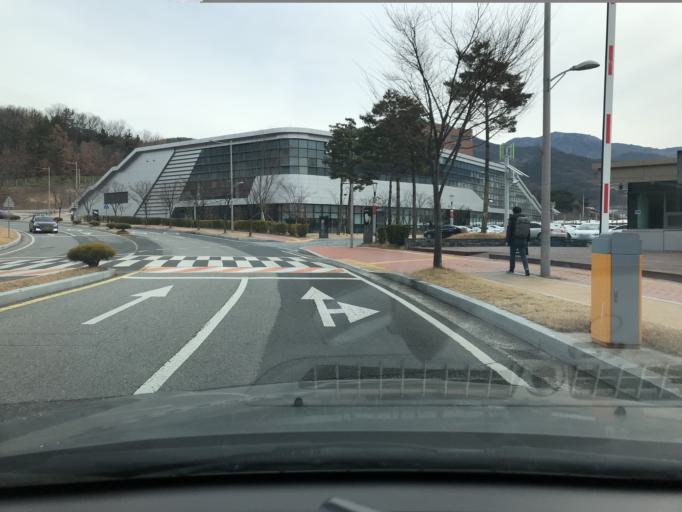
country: KR
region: Daegu
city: Hwawon
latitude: 35.7004
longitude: 128.4582
